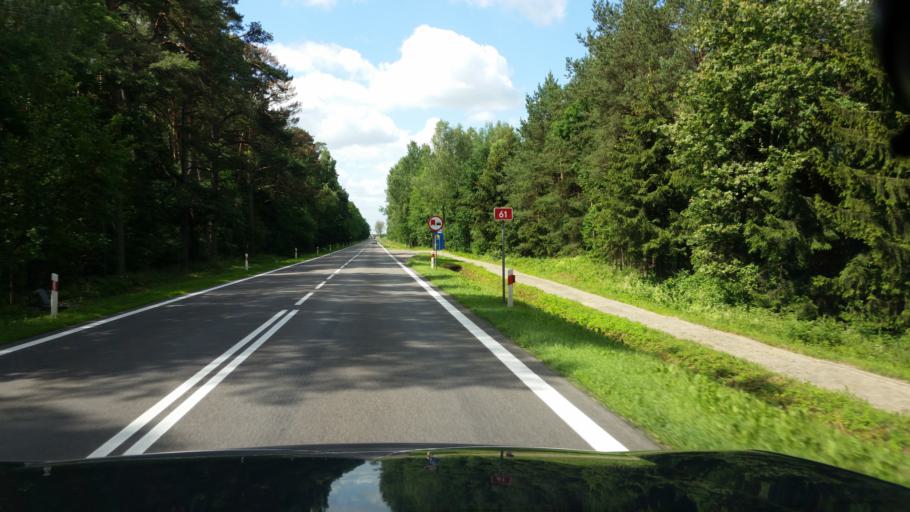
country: PL
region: Podlasie
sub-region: Powiat grajewski
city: Rajgrod
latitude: 53.6945
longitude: 22.6425
